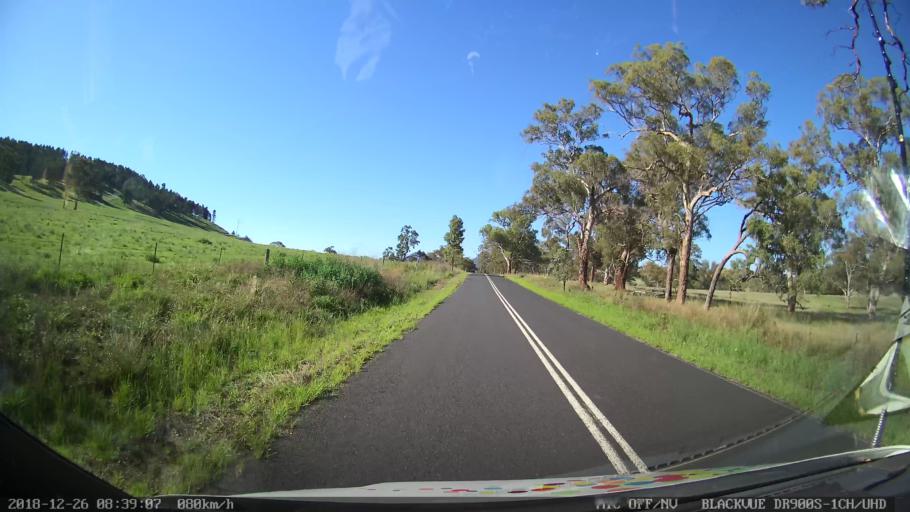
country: AU
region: New South Wales
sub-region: Upper Hunter Shire
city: Merriwa
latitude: -32.4497
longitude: 150.0765
